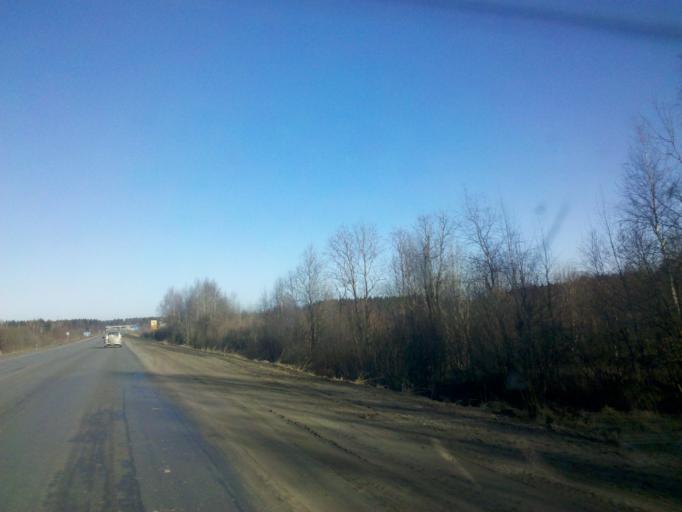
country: RU
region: Republic of Karelia
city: Shuya
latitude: 61.8313
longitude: 34.2088
